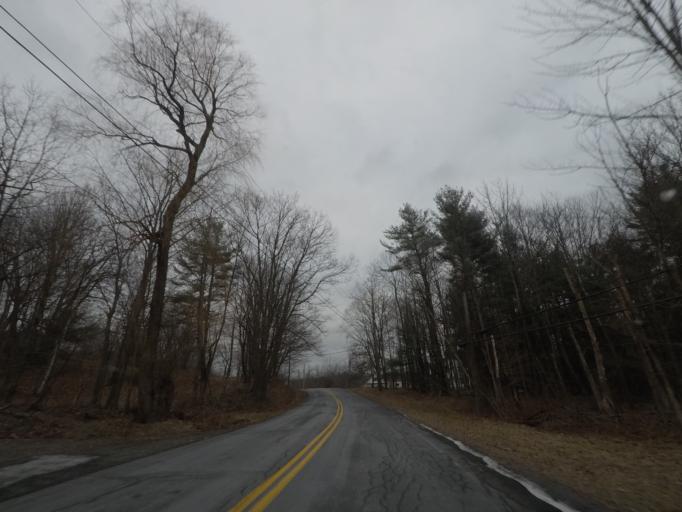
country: US
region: New York
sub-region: Rensselaer County
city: Poestenkill
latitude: 42.7623
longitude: -73.5073
